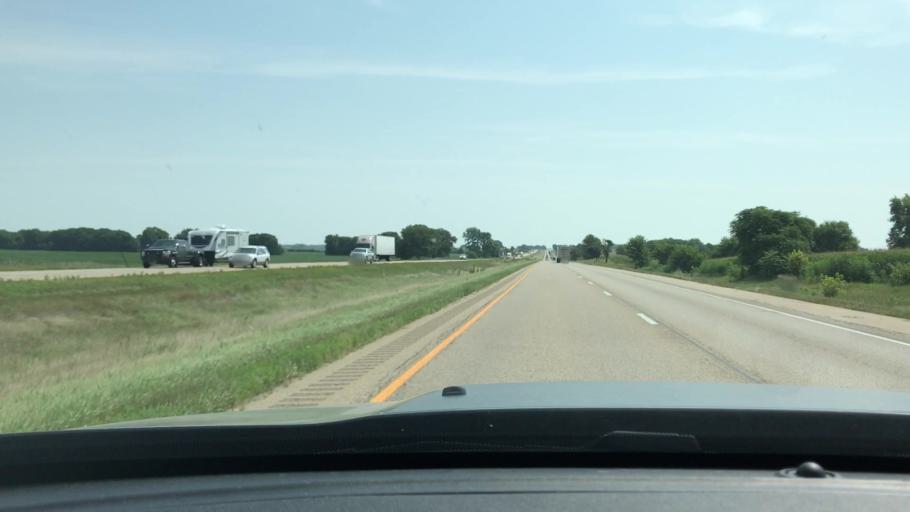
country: US
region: Illinois
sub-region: Henry County
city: Kewanee
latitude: 41.3865
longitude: -89.7641
